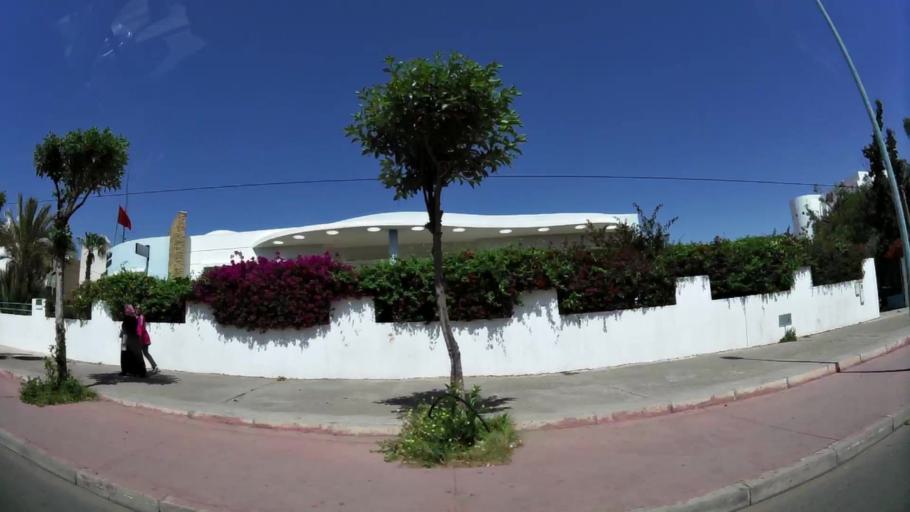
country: MA
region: Souss-Massa-Draa
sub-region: Agadir-Ida-ou-Tnan
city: Agadir
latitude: 30.4111
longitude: -9.5831
